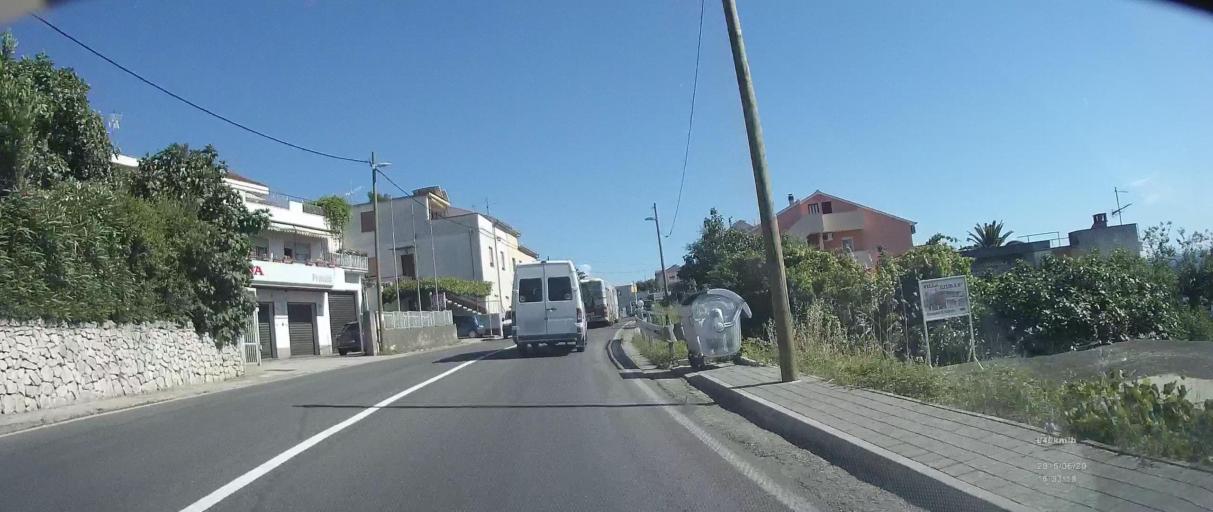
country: HR
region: Splitsko-Dalmatinska
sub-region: Grad Split
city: Stobrec
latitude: 43.4973
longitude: 16.5370
